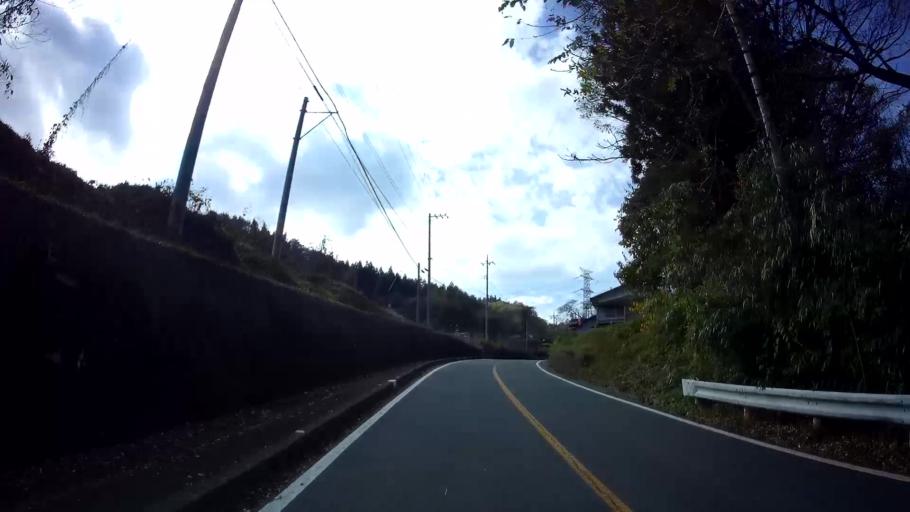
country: JP
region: Gunma
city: Nakanojomachi
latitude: 36.5069
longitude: 138.7447
